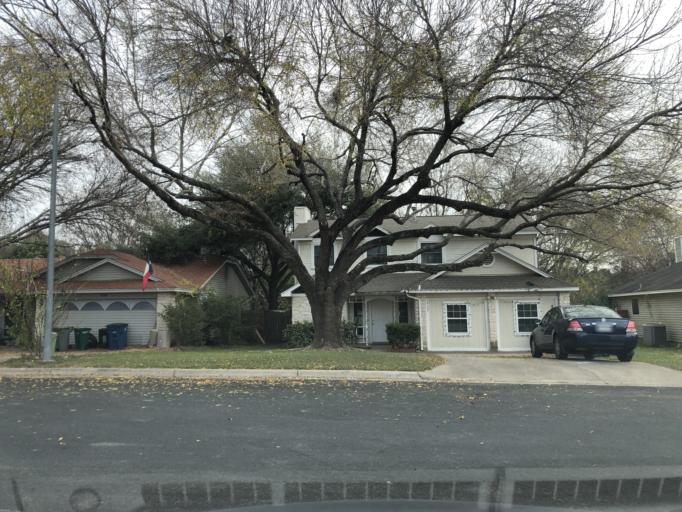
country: US
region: Texas
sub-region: Travis County
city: Wells Branch
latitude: 30.4224
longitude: -97.6848
